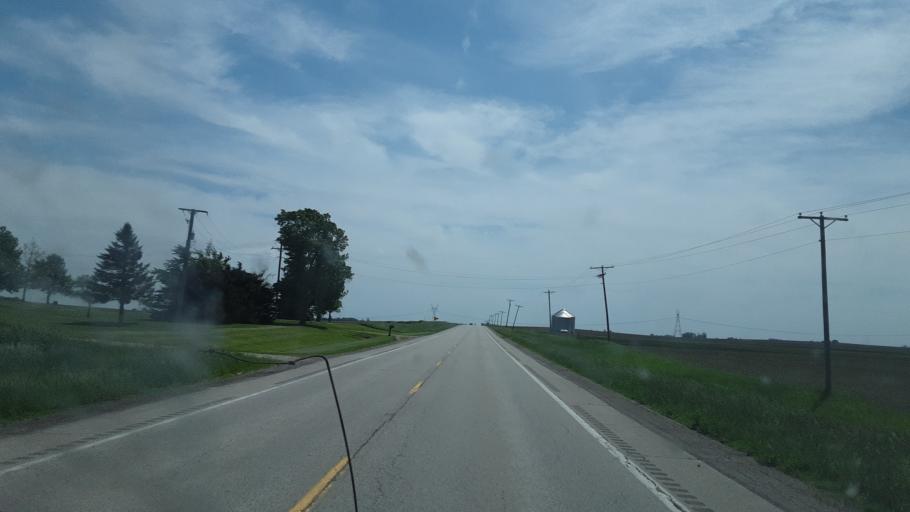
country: US
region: Illinois
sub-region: McLean County
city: Heyworth
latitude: 40.3122
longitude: -88.9467
